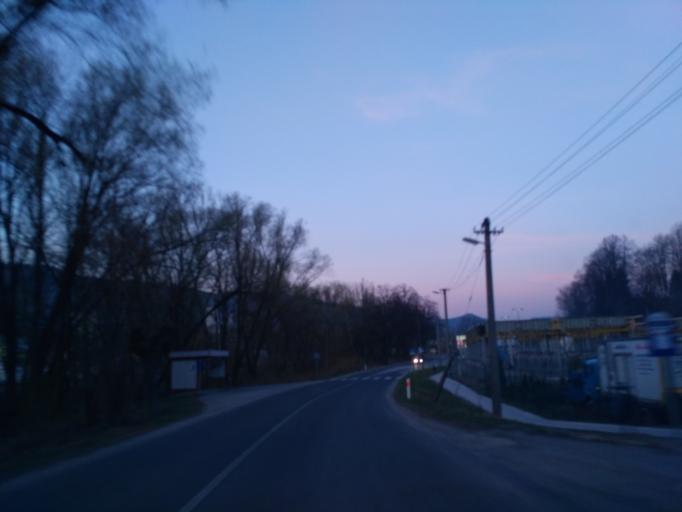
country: SK
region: Kosicky
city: Gelnica
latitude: 48.8538
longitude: 20.9404
